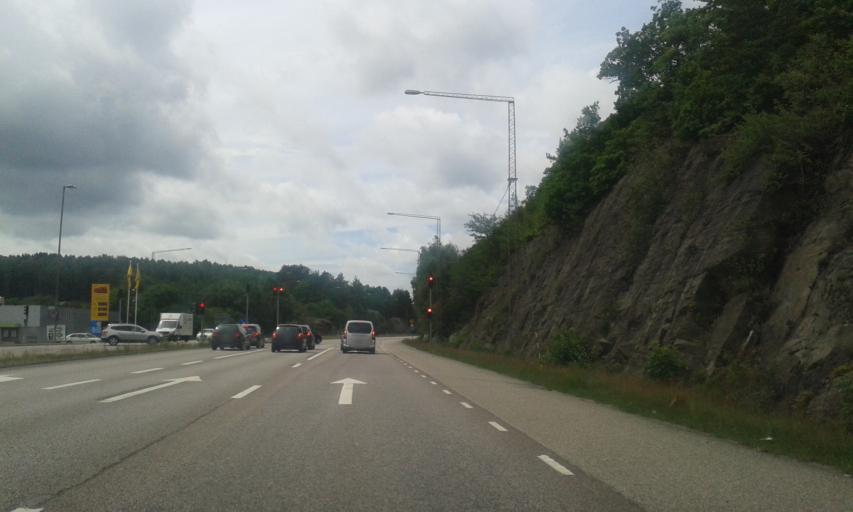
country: SE
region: Vaestra Goetaland
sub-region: Kungalvs Kommun
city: Kungalv
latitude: 57.8724
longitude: 11.9502
